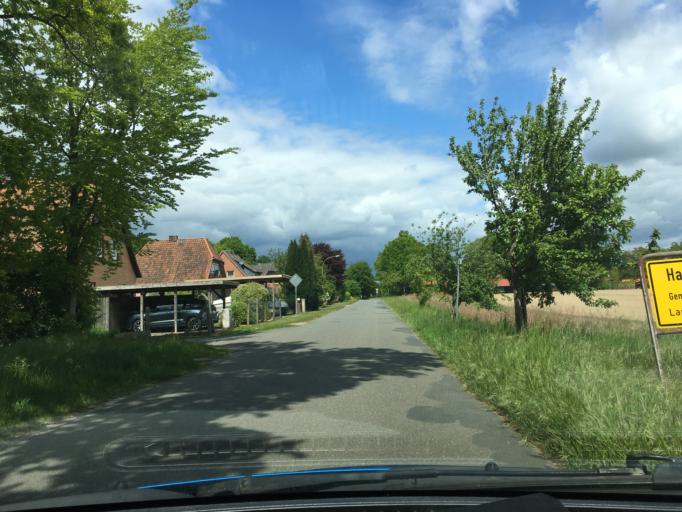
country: DE
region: Lower Saxony
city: Suderburg
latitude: 52.9137
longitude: 10.4576
